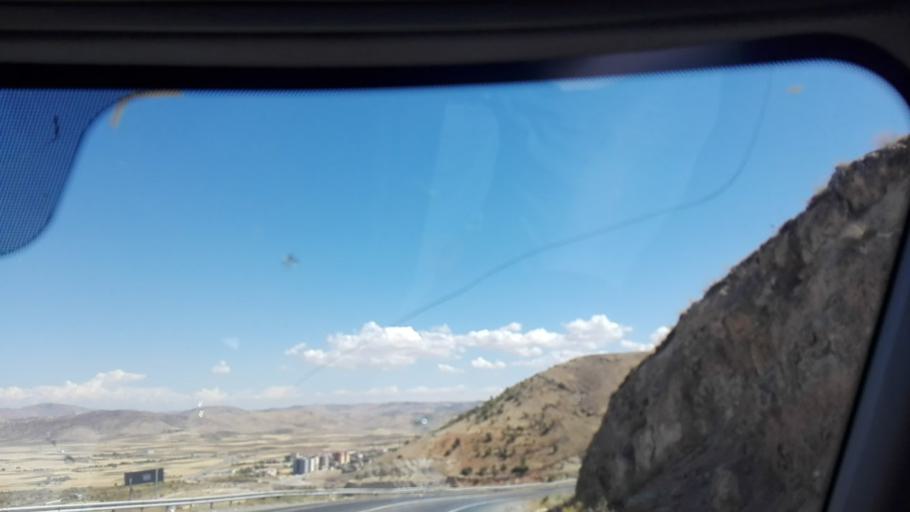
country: TR
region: Batman
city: Gerdzhyush
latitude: 37.5629
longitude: 41.3637
